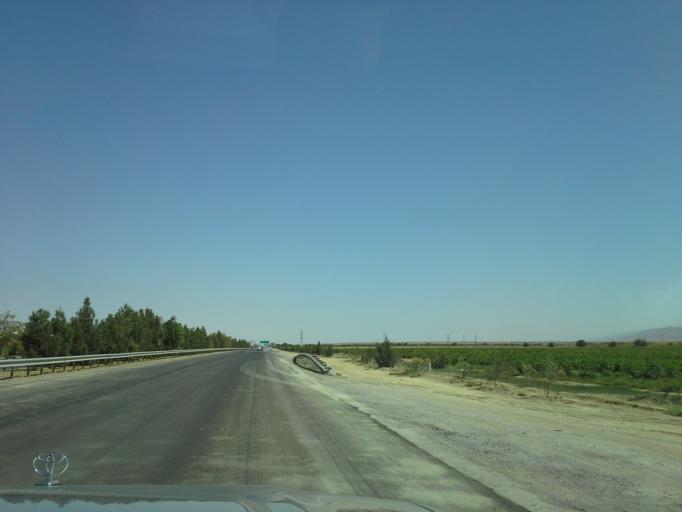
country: TM
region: Ahal
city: Annau
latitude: 37.9059
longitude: 58.5301
